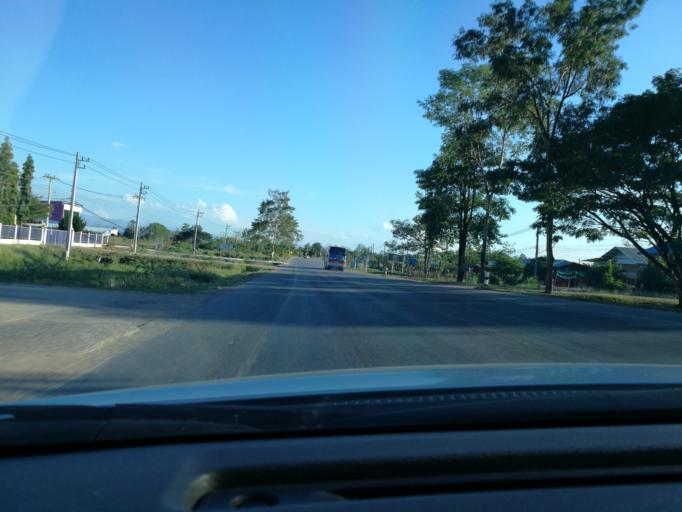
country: TH
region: Phitsanulok
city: Nakhon Thai
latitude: 17.0566
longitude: 100.8101
